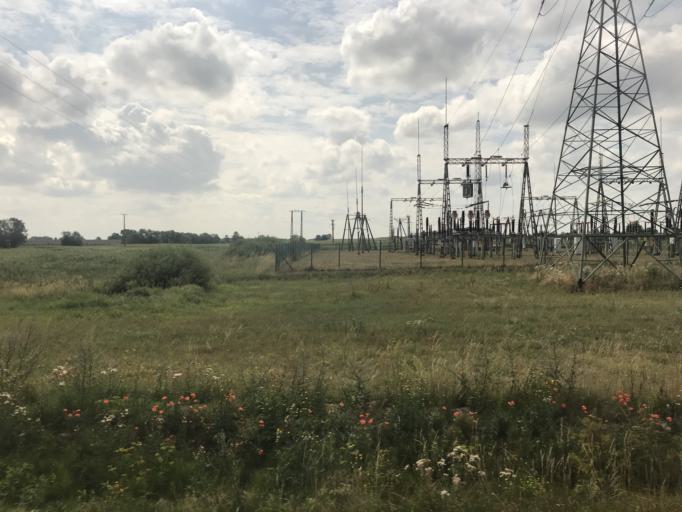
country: PL
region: Greater Poland Voivodeship
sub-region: Powiat gnieznienski
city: Lubowo
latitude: 52.5009
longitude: 17.4424
